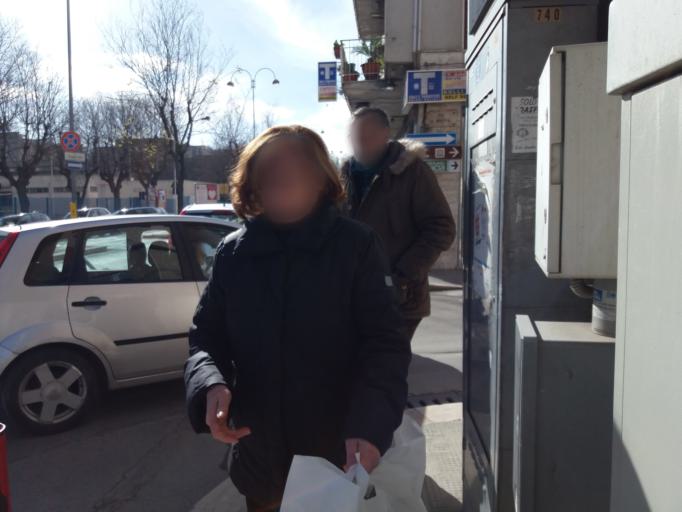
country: IT
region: Apulia
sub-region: Provincia di Barletta - Andria - Trani
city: Andria
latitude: 41.2258
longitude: 16.3067
